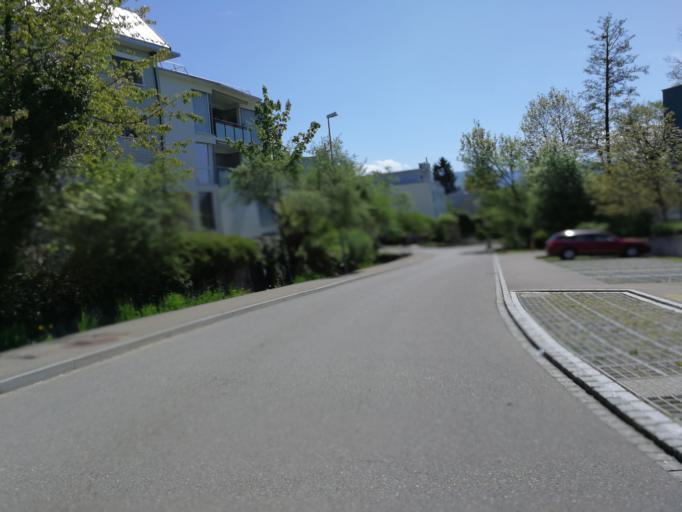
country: CH
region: Zurich
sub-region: Bezirk Meilen
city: Uetikon
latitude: 47.2607
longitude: 8.6831
